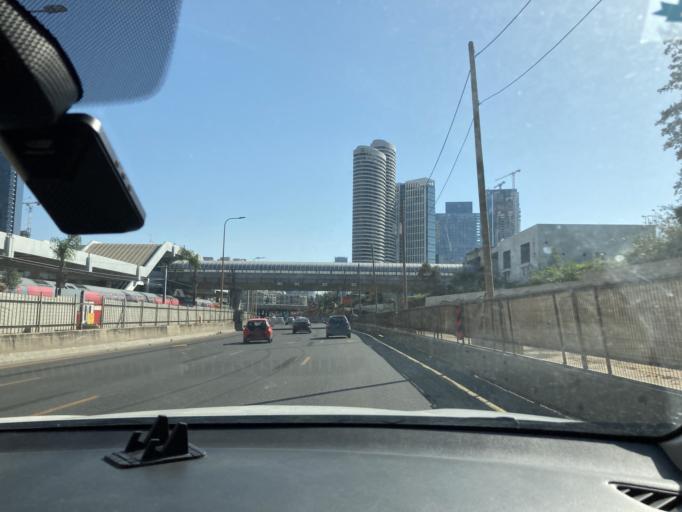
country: IL
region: Tel Aviv
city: Ramat Gan
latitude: 32.0848
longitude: 34.7980
